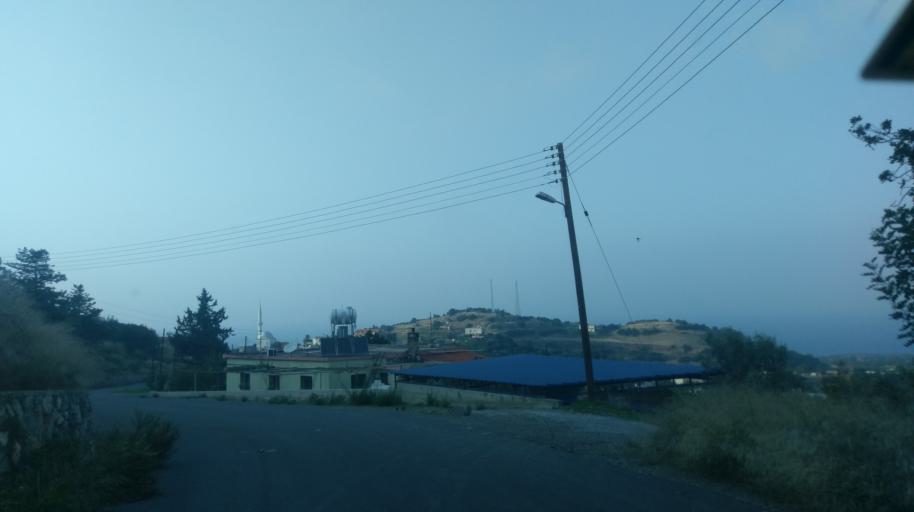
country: CY
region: Ammochostos
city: Trikomo
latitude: 35.3937
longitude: 33.8600
